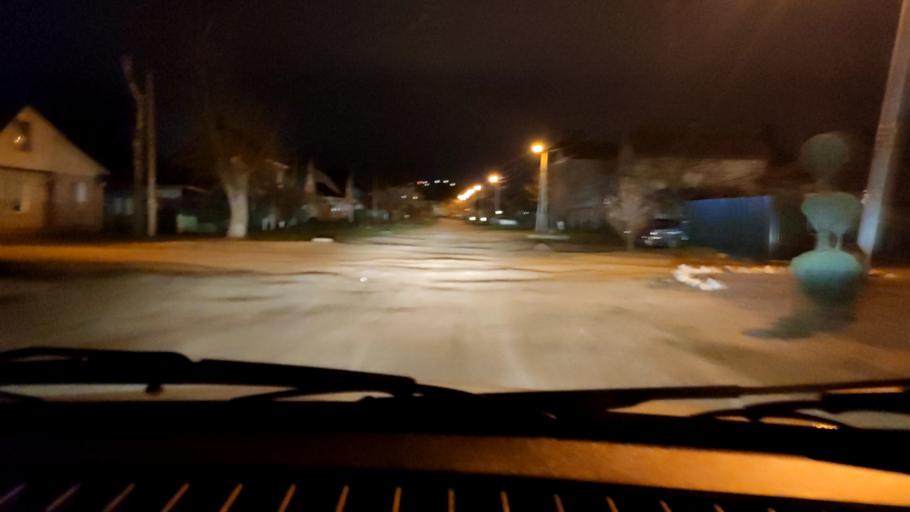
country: RU
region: Voronezj
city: Somovo
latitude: 51.7310
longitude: 39.2682
